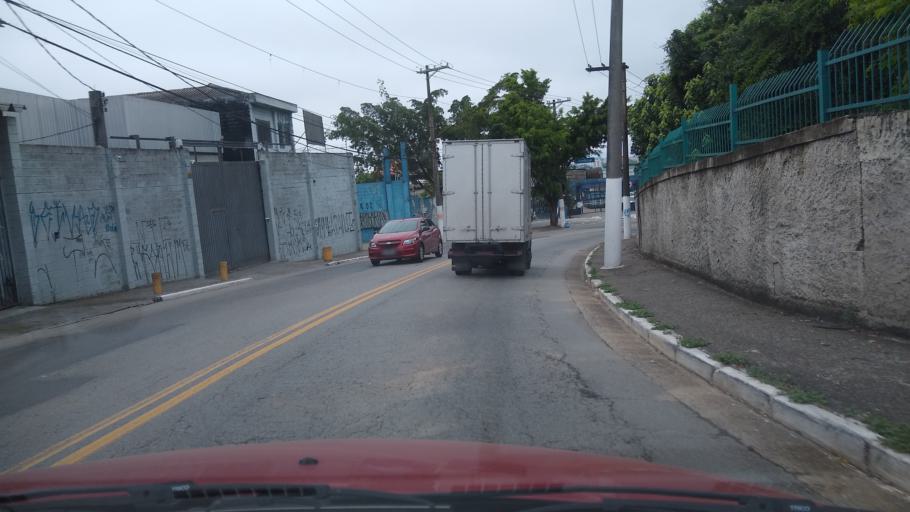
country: BR
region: Sao Paulo
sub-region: Diadema
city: Diadema
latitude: -23.6425
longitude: -46.6128
